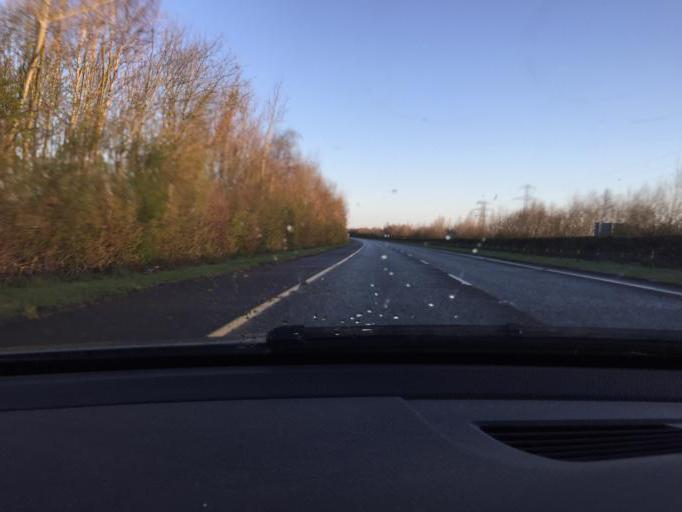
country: IE
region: Leinster
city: Balrothery
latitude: 53.5879
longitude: -6.2126
